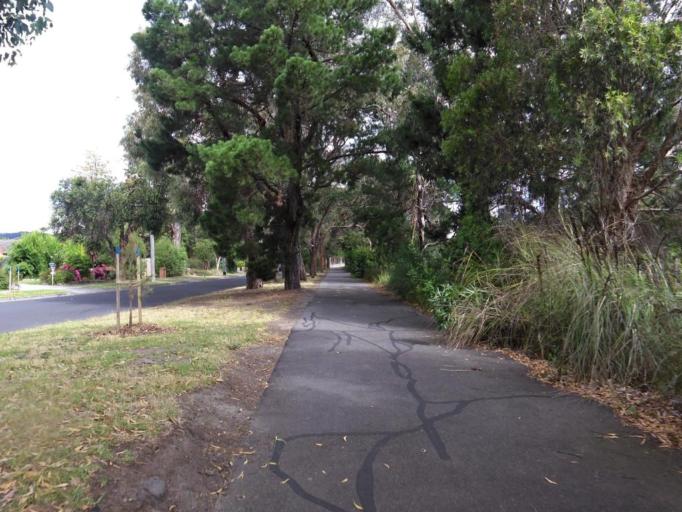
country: AU
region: Victoria
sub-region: Knox
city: Boronia
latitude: -37.8549
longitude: 145.2811
